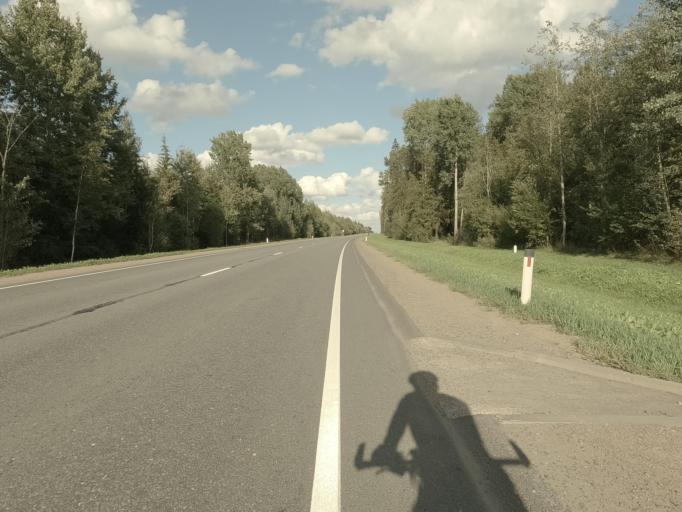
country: RU
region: Leningrad
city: Nikol'skoye
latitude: 59.6679
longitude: 30.8893
